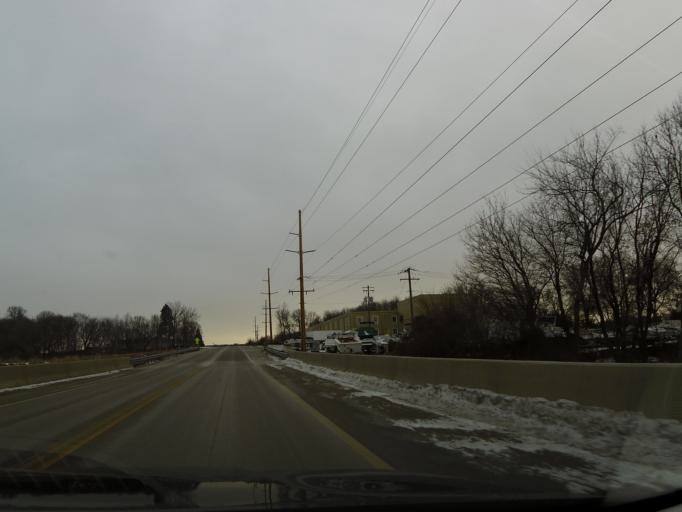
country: US
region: Minnesota
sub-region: Carver County
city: Waconia
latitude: 44.8822
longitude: -93.8153
